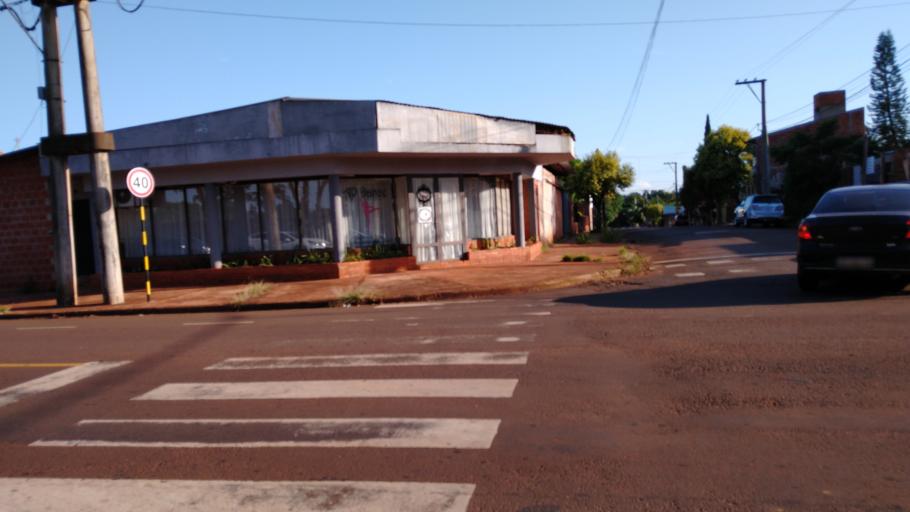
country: AR
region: Misiones
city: Puerto Rico
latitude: -26.8064
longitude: -55.0274
